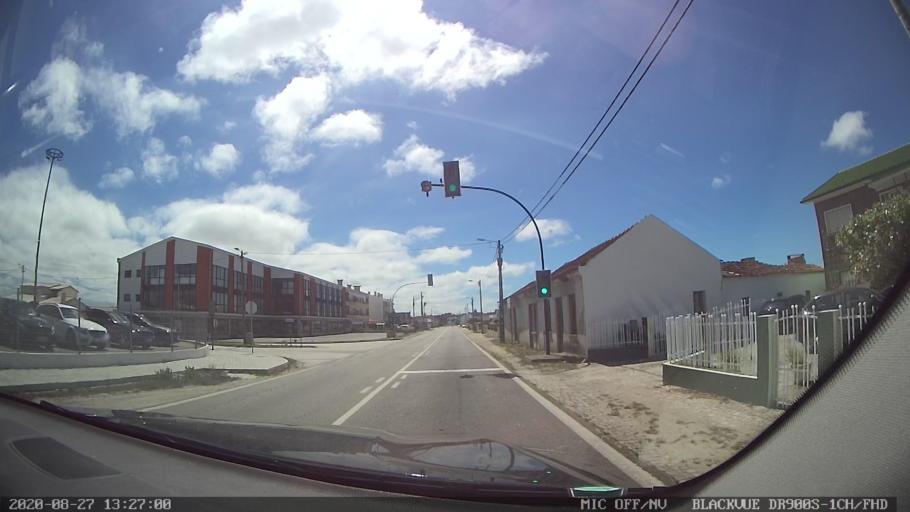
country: PT
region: Aveiro
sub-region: Vagos
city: Vagos
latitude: 40.5336
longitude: -8.6777
